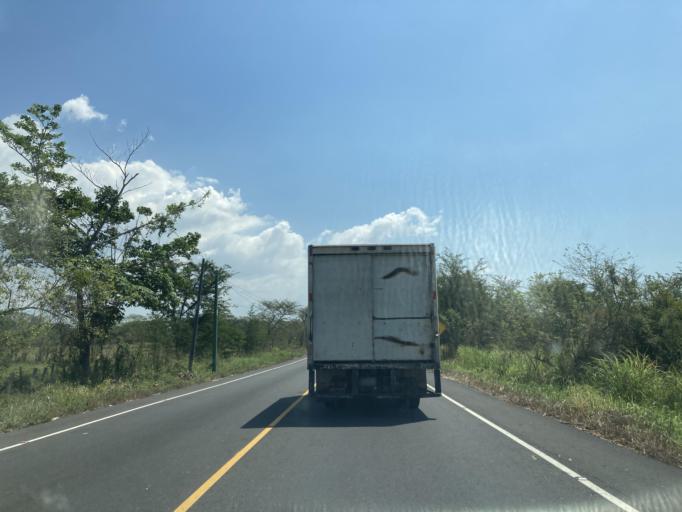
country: GT
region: Santa Rosa
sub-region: Municipio de Taxisco
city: Taxisco
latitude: 14.0941
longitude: -90.5874
